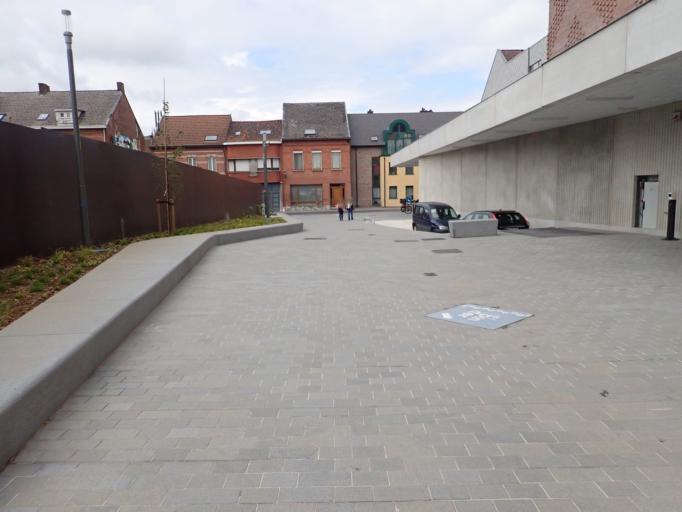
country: BE
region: Flanders
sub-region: Provincie Antwerpen
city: Puurs
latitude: 51.0752
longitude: 4.2746
